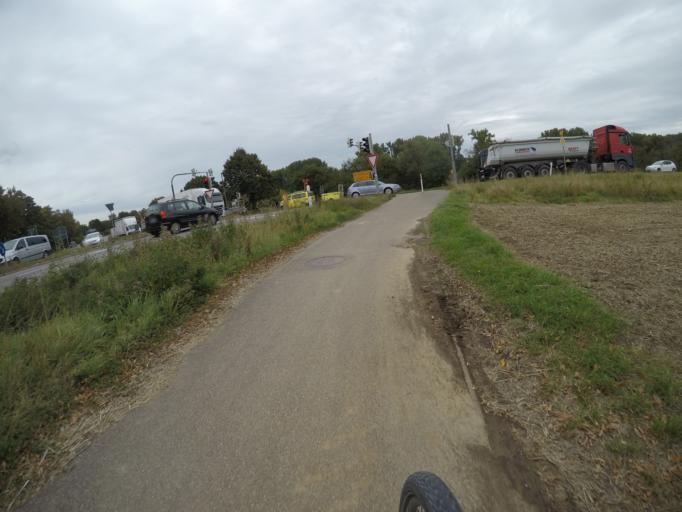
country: DE
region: Baden-Wuerttemberg
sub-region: Regierungsbezirk Stuttgart
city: Vaihingen an der Enz
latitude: 48.9224
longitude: 8.9727
